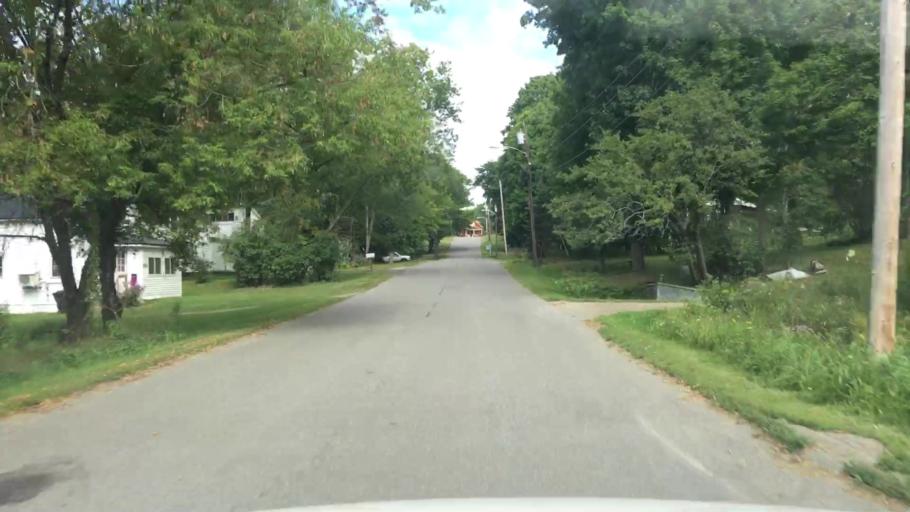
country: US
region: Maine
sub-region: Piscataquis County
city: Dover-Foxcroft
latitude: 45.1886
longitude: -69.2225
